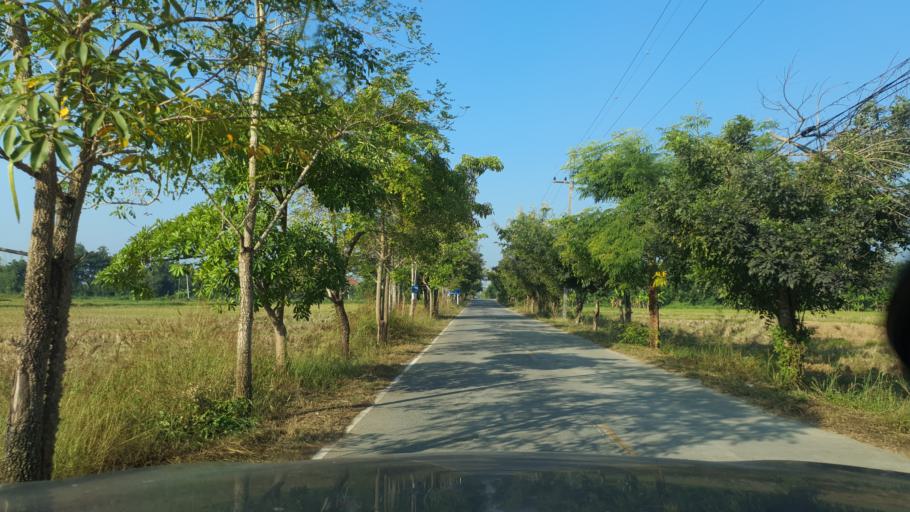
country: TH
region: Chiang Mai
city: San Kamphaeng
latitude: 18.7213
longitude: 99.0844
